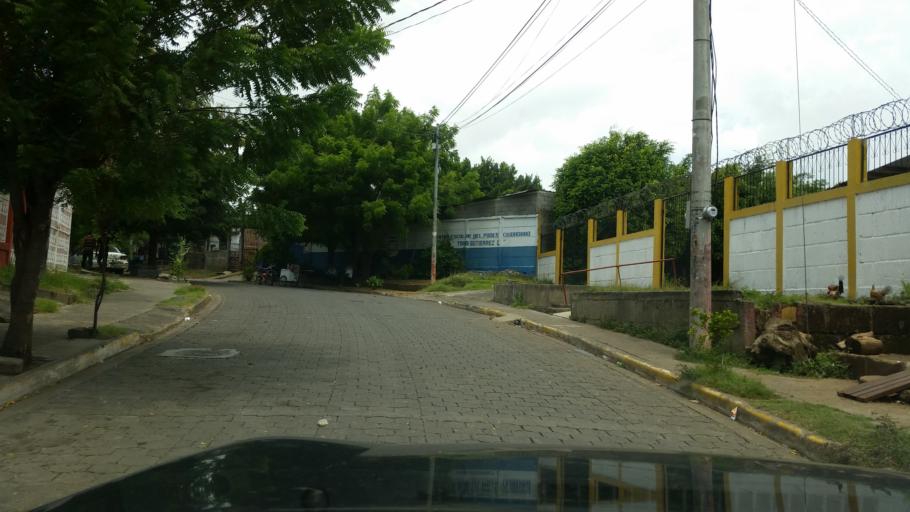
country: NI
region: Managua
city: Managua
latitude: 12.1476
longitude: -86.2162
